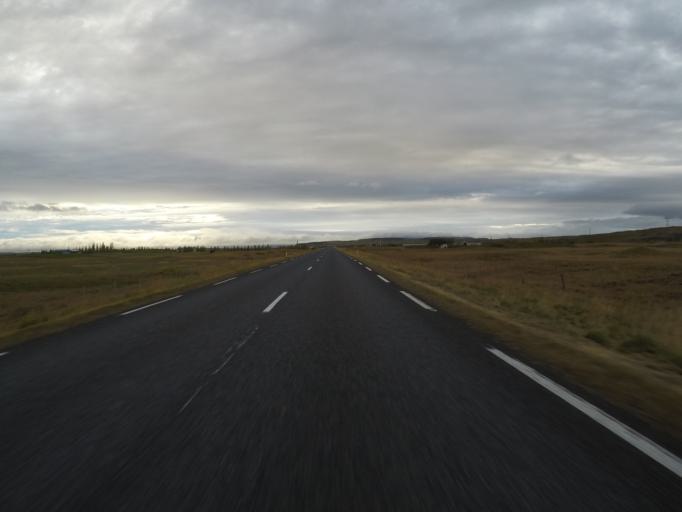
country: IS
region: South
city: Vestmannaeyjar
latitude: 64.0411
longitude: -20.2130
